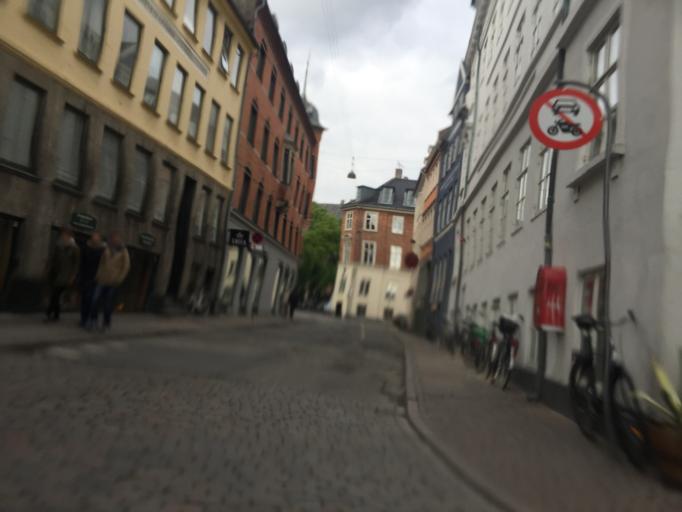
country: DK
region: Capital Region
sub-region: Kobenhavn
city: Copenhagen
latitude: 55.6779
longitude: 12.5807
